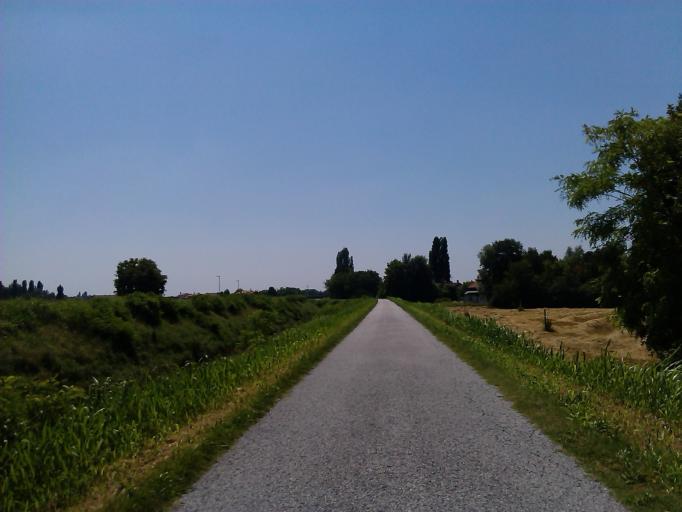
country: IT
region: Veneto
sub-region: Provincia di Padova
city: Loreggiola
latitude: 45.6040
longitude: 11.9320
